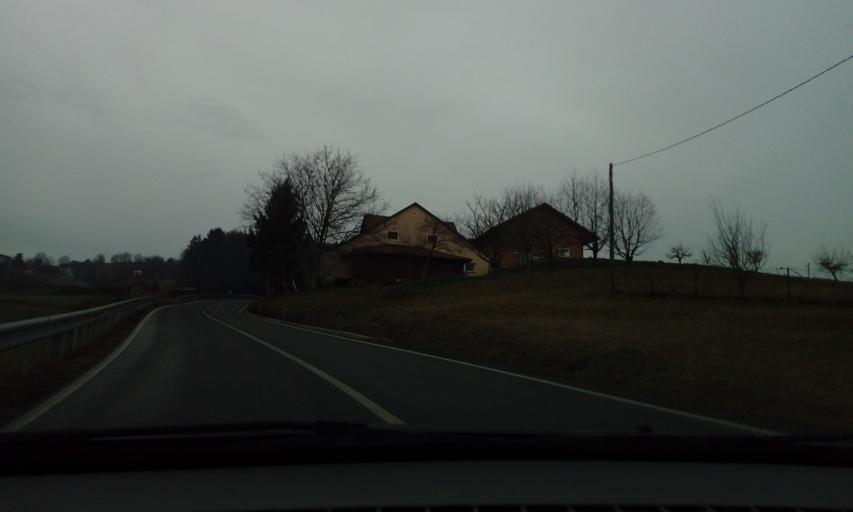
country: SI
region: Smarje pri Jelsah
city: Smarje pri Jelsah
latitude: 46.2306
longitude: 15.4933
